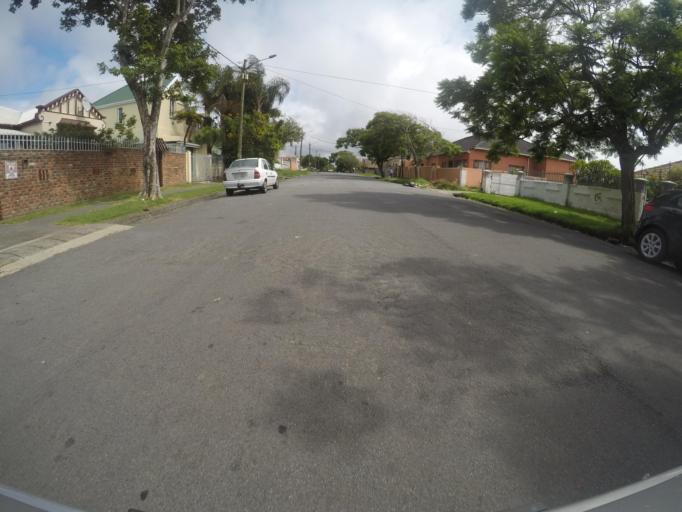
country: ZA
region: Eastern Cape
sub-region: Buffalo City Metropolitan Municipality
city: East London
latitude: -32.9996
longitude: 27.9078
